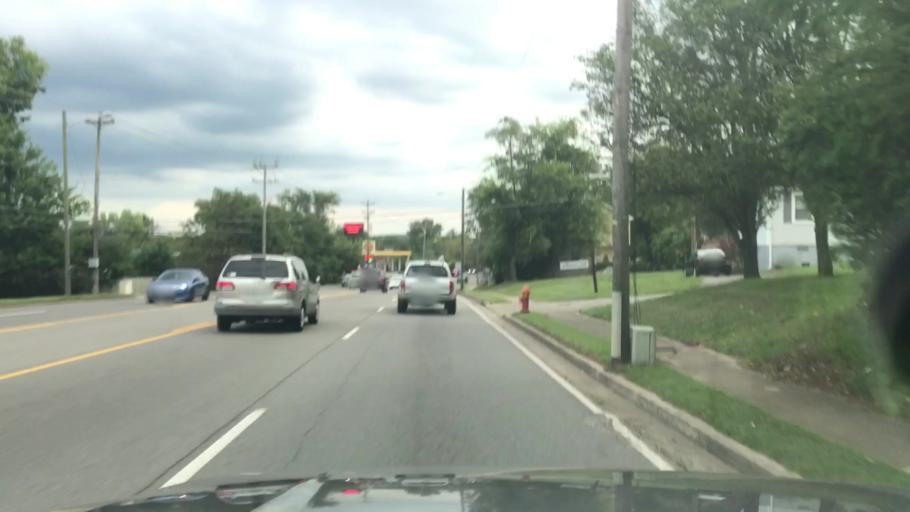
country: US
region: Tennessee
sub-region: Davidson County
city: Belle Meade
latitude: 36.1406
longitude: -86.8575
